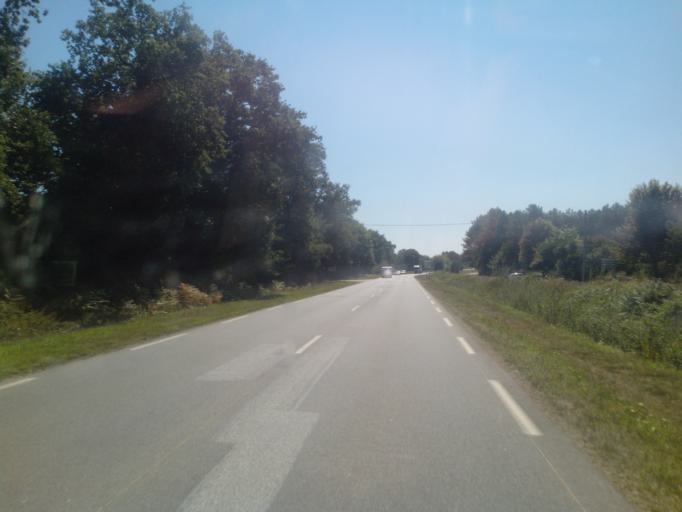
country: FR
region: Brittany
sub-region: Departement du Morbihan
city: Molac
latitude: 47.7396
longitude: -2.4378
